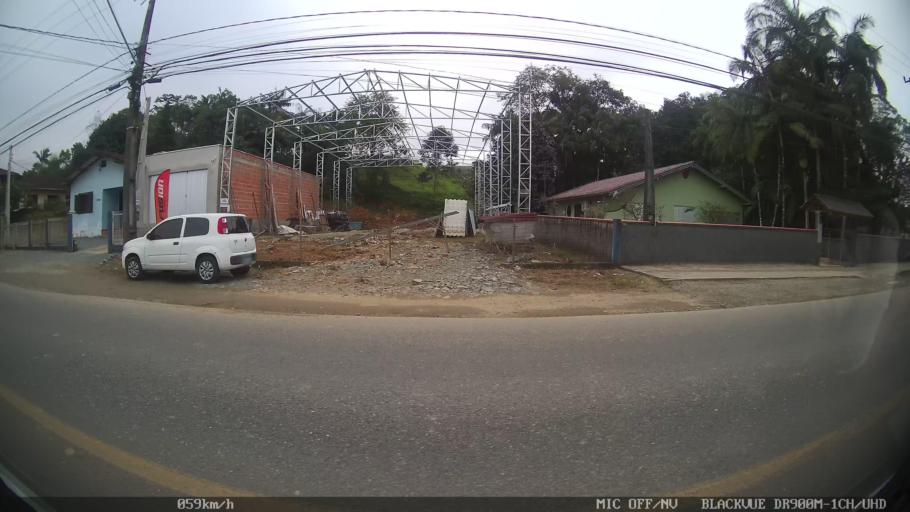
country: BR
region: Santa Catarina
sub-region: Joinville
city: Joinville
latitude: -26.3383
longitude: -48.8804
